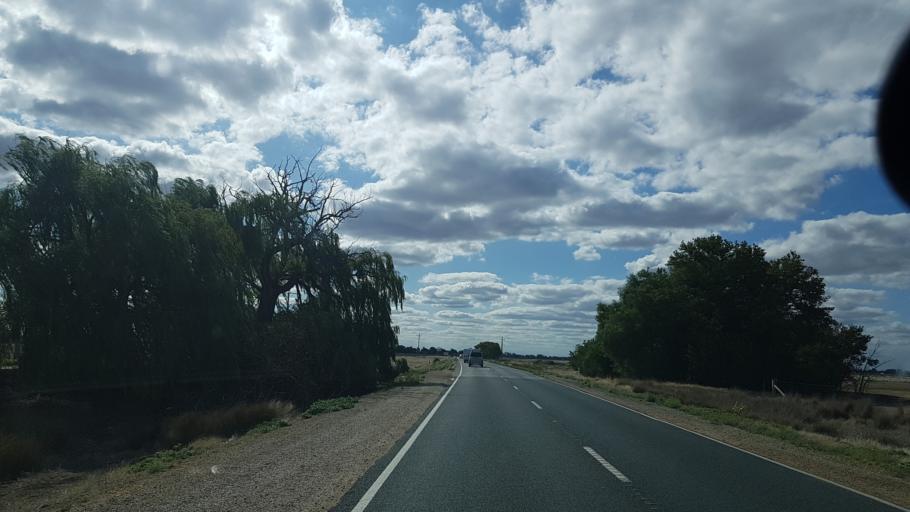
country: AU
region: Victoria
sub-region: Swan Hill
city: Swan Hill
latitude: -35.7916
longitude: 143.9470
